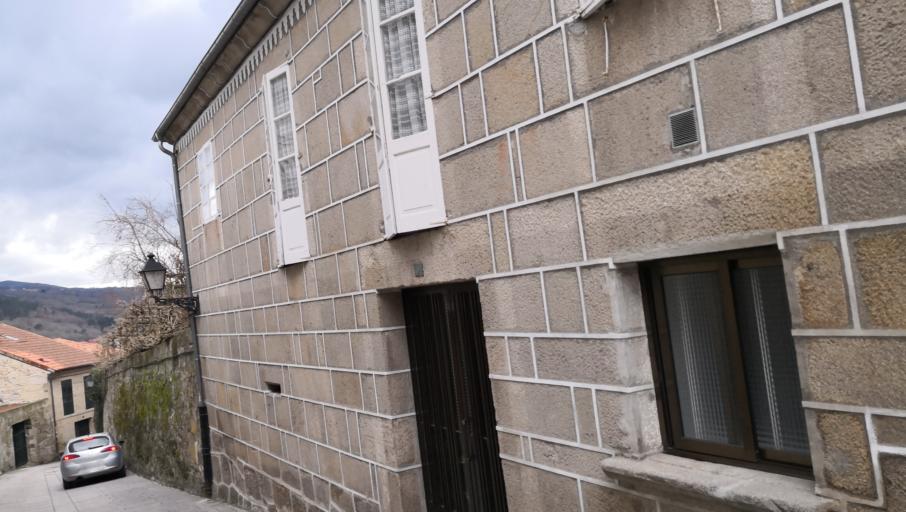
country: ES
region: Galicia
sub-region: Provincia de Ourense
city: Allariz
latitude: 42.1906
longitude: -7.8006
